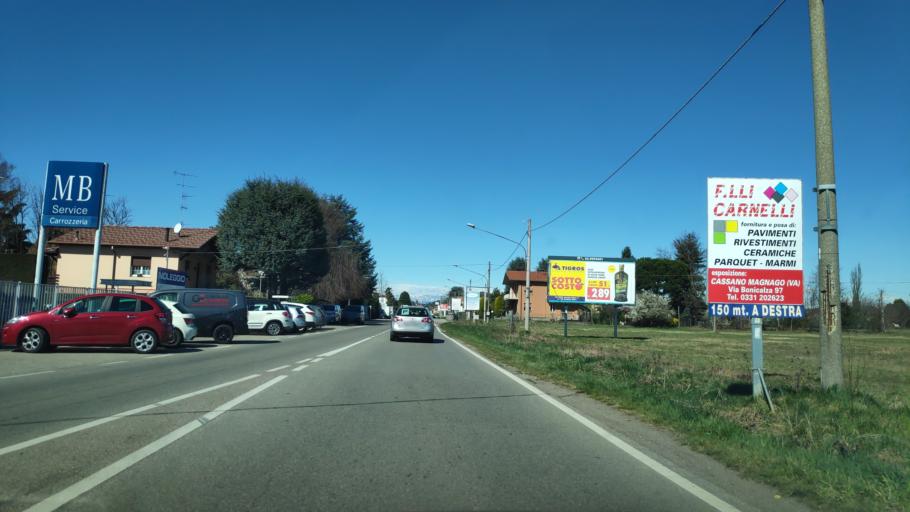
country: IT
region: Lombardy
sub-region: Provincia di Varese
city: Fagnano Olona-Bergoro
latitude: 45.6641
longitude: 8.8402
